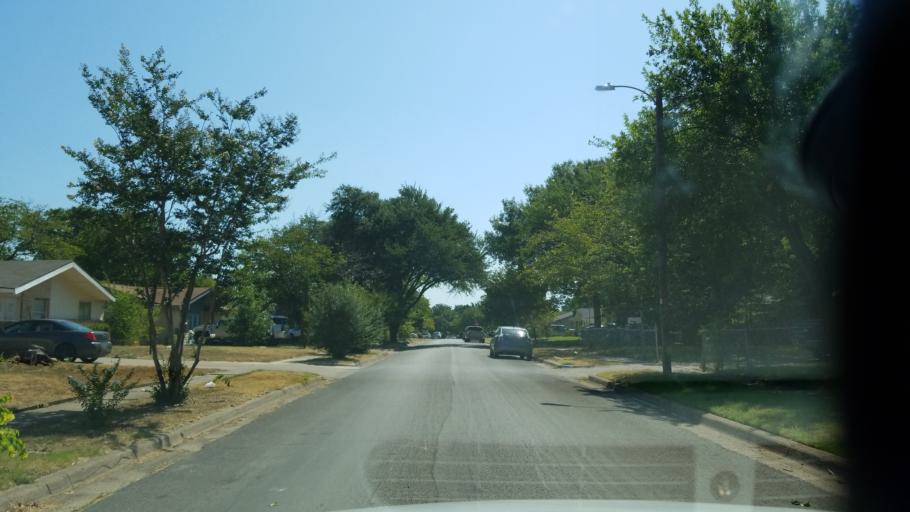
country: US
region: Texas
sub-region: Dallas County
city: Duncanville
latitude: 32.6421
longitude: -96.9025
